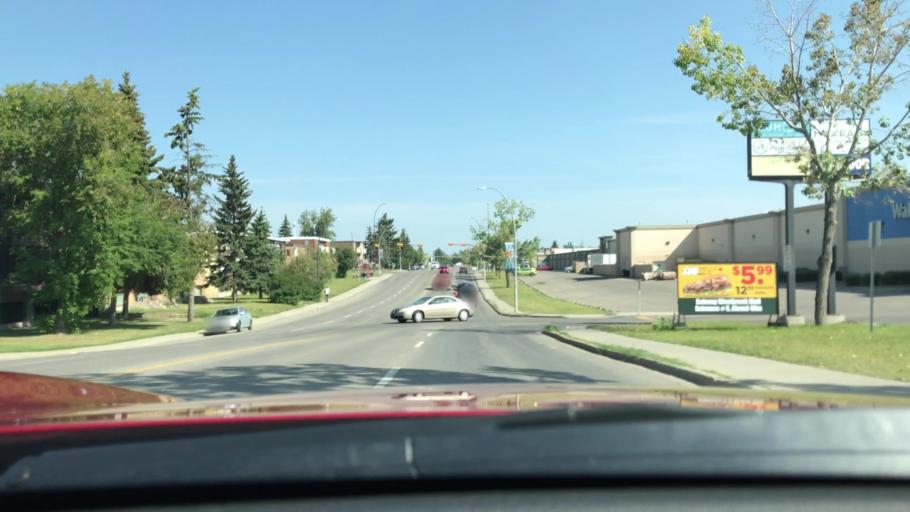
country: CA
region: Alberta
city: Calgary
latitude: 51.0396
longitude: -114.1413
